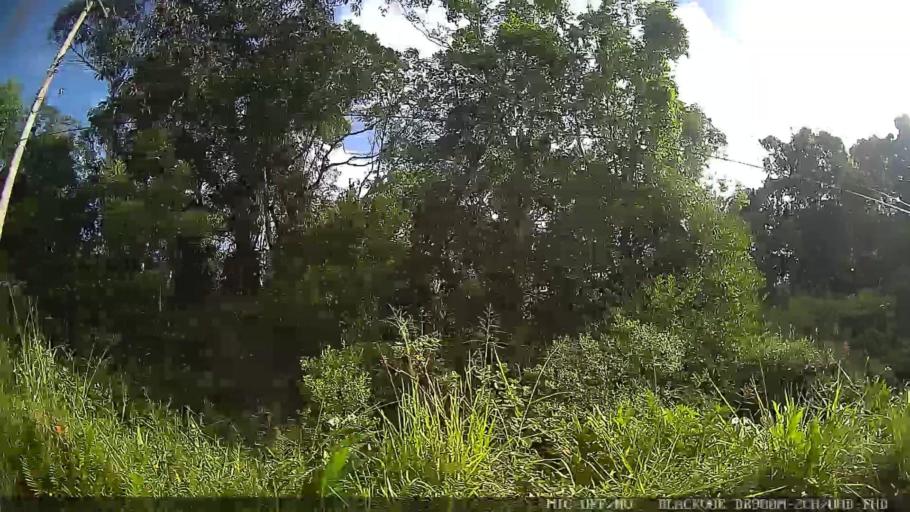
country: BR
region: Sao Paulo
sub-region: Itanhaem
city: Itanhaem
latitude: -24.1983
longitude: -46.8945
